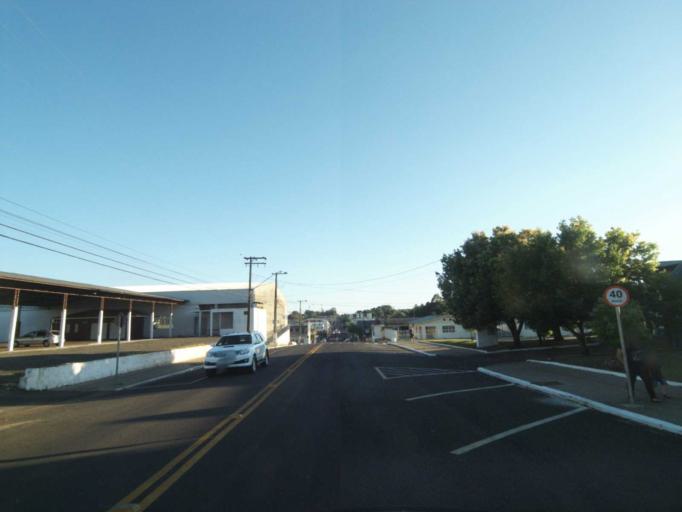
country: BR
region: Parana
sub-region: Coronel Vivida
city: Coronel Vivida
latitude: -25.9652
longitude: -52.8161
